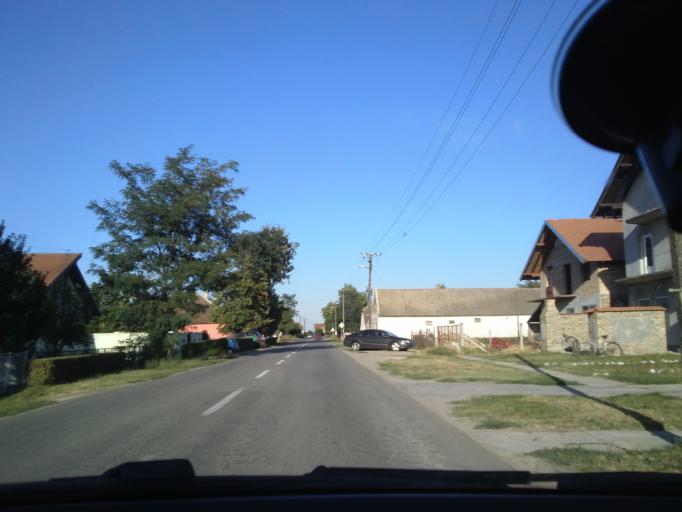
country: RS
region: Autonomna Pokrajina Vojvodina
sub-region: Zapadnobacki Okrug
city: Odzaci
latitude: 45.4507
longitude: 19.3388
